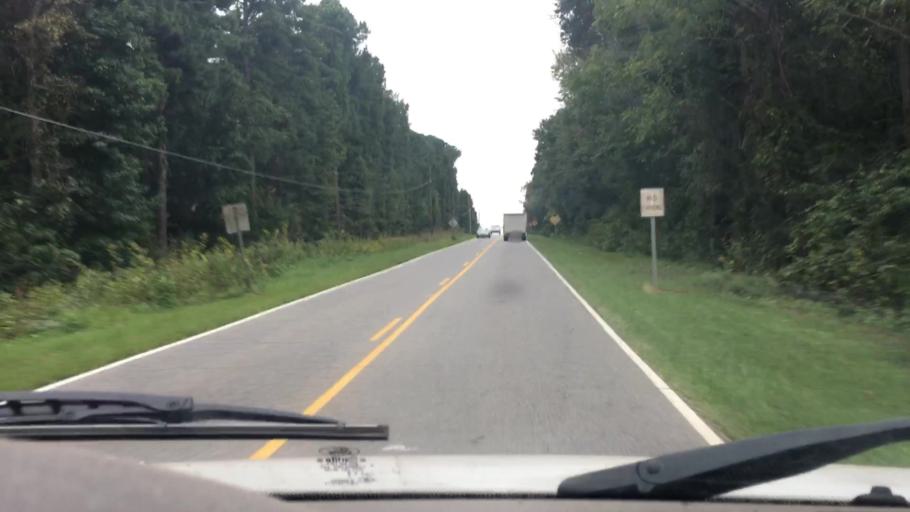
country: US
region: North Carolina
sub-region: Catawba County
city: Lake Norman of Catawba
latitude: 35.5640
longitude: -80.9904
